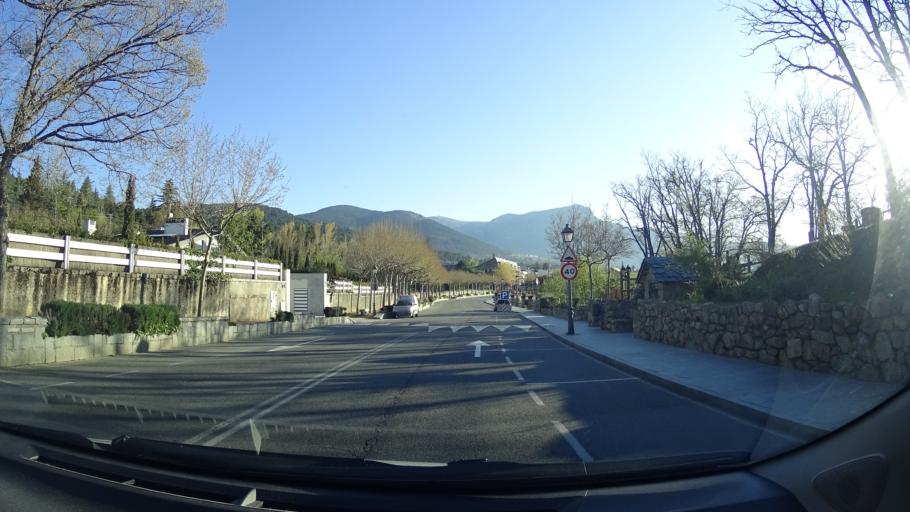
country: ES
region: Madrid
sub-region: Provincia de Madrid
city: Navacerrada
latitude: 40.7260
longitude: -4.0192
